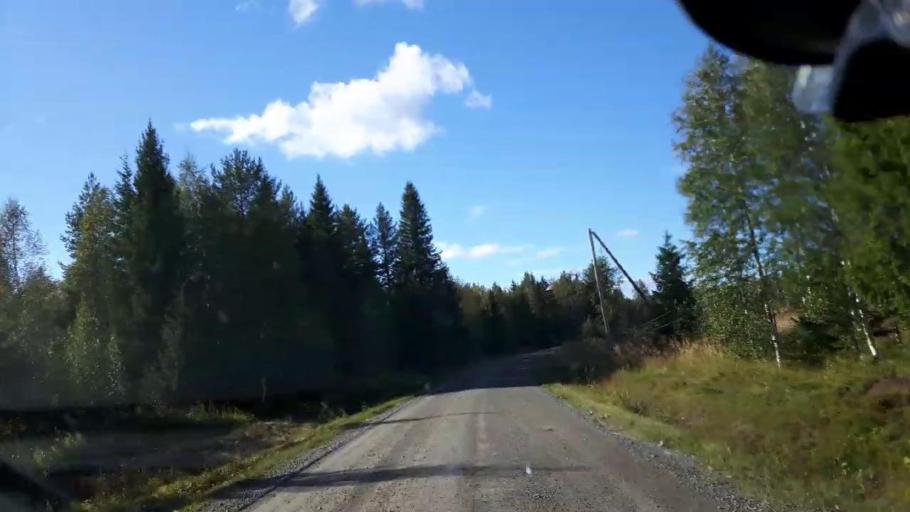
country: SE
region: Jaemtland
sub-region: Ragunda Kommun
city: Hammarstrand
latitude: 63.4683
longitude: 16.1831
